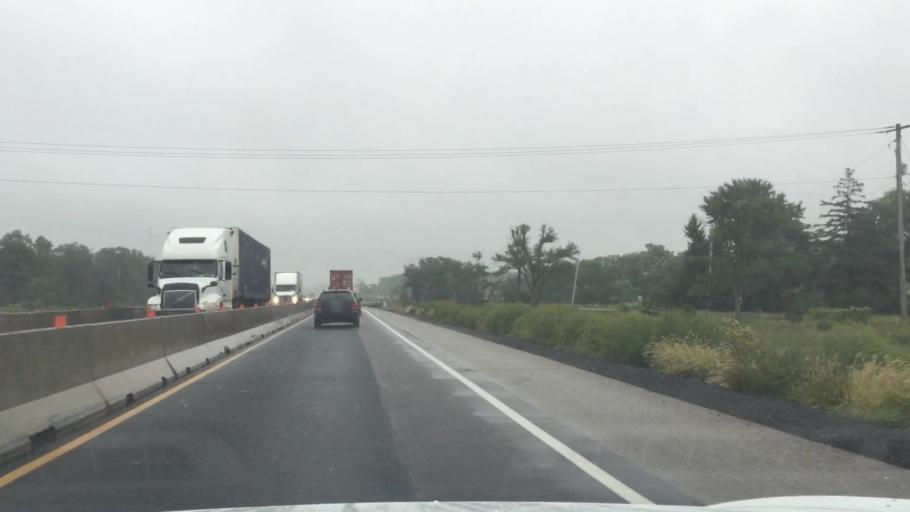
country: CA
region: Ontario
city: St. Thomas
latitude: 42.8165
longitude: -81.3152
